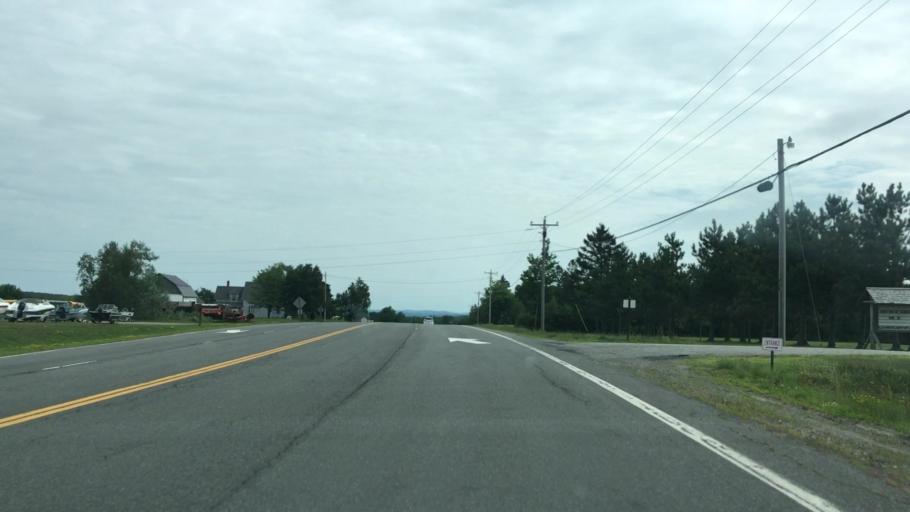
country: US
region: Maine
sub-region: Washington County
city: Calais
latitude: 45.0922
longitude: -67.4773
